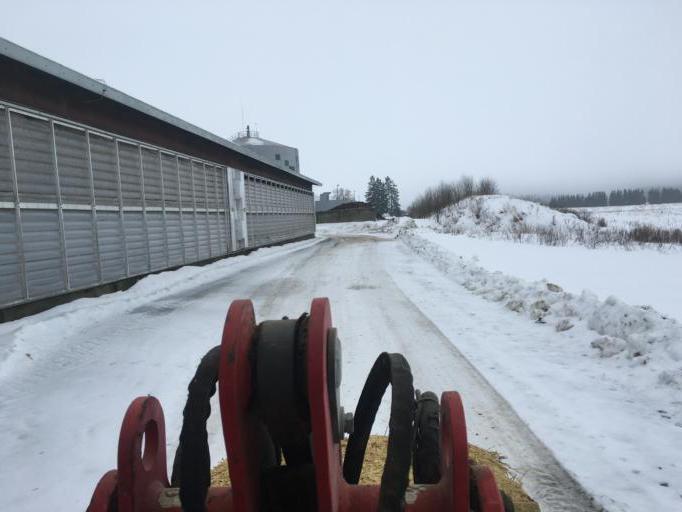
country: EE
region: Jaervamaa
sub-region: Jaerva-Jaani vald
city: Jarva-Jaani
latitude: 59.1502
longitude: 25.7345
